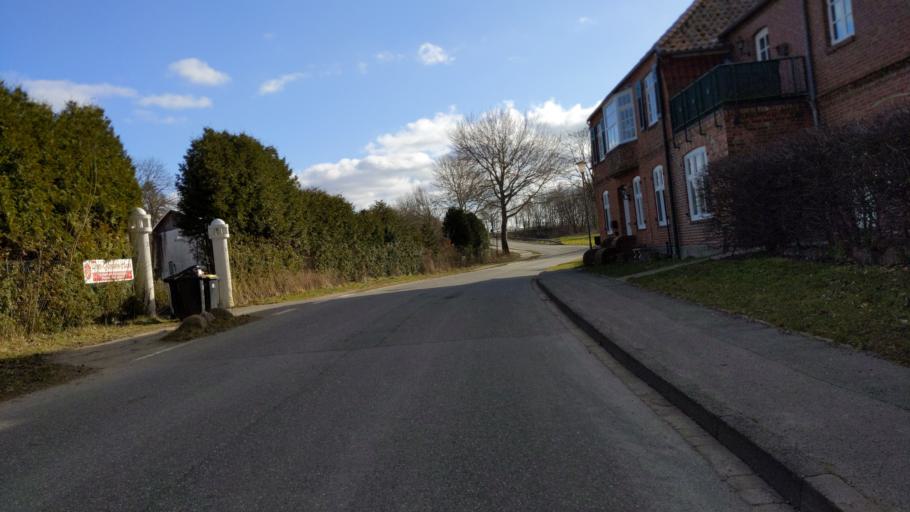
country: DE
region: Schleswig-Holstein
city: Scharbeutz
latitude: 54.0106
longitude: 10.7537
